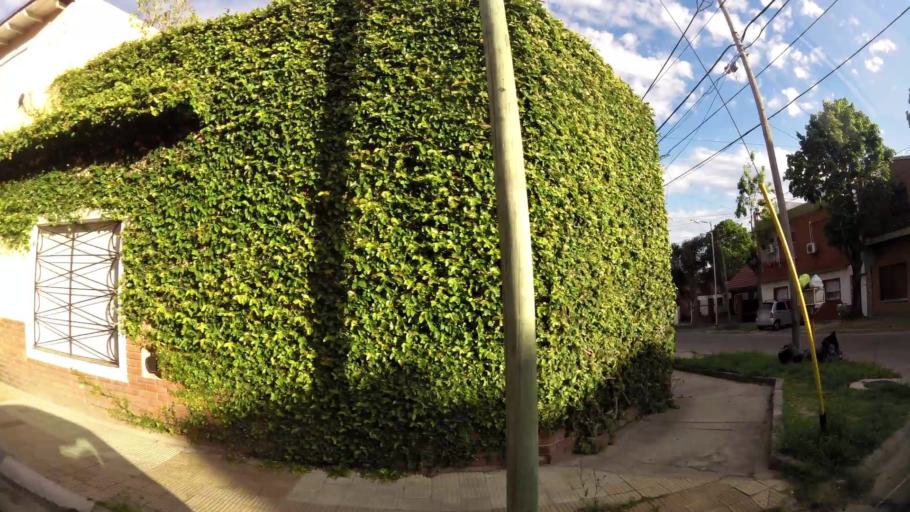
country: AR
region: Buenos Aires
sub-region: Partido de Avellaneda
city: Avellaneda
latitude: -34.6871
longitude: -58.3474
